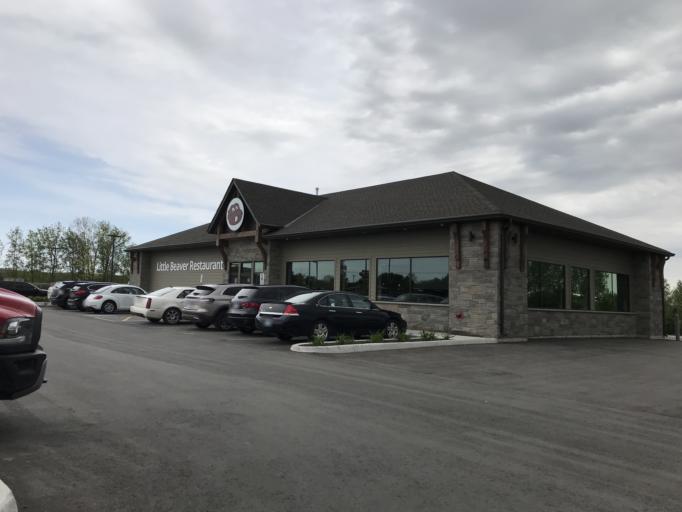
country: CA
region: Ontario
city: Delaware
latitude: 42.9437
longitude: -81.4322
